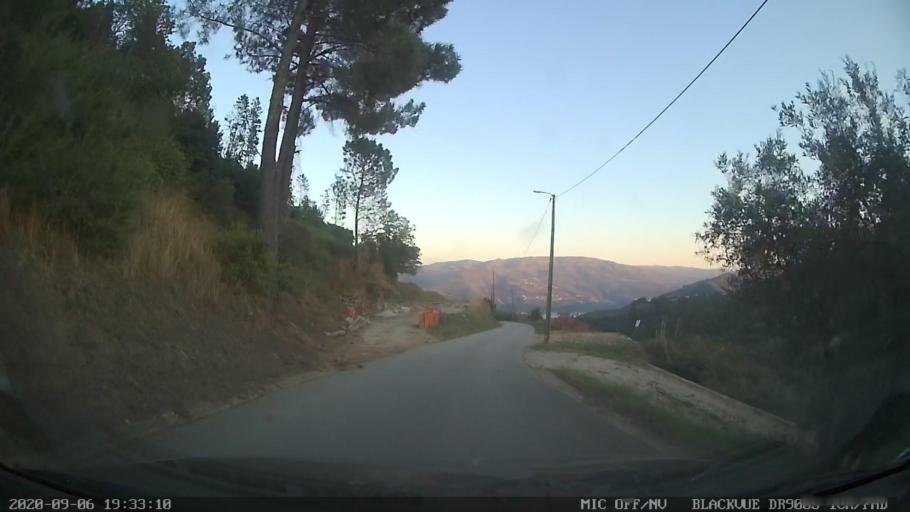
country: PT
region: Vila Real
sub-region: Mesao Frio
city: Mesao Frio
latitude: 41.1763
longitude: -7.9002
